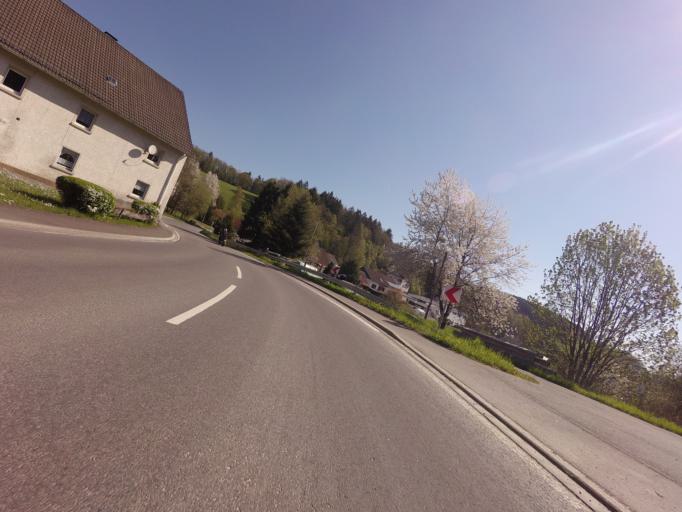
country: DE
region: North Rhine-Westphalia
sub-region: Regierungsbezirk Arnsberg
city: Drolshagen
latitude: 51.0806
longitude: 7.7912
